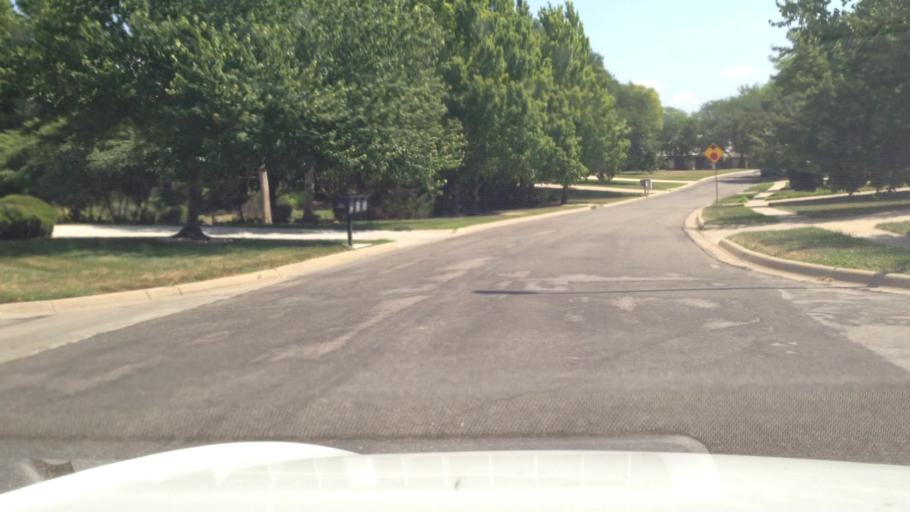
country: US
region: Kansas
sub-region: Douglas County
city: Lawrence
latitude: 38.9537
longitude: -95.3041
